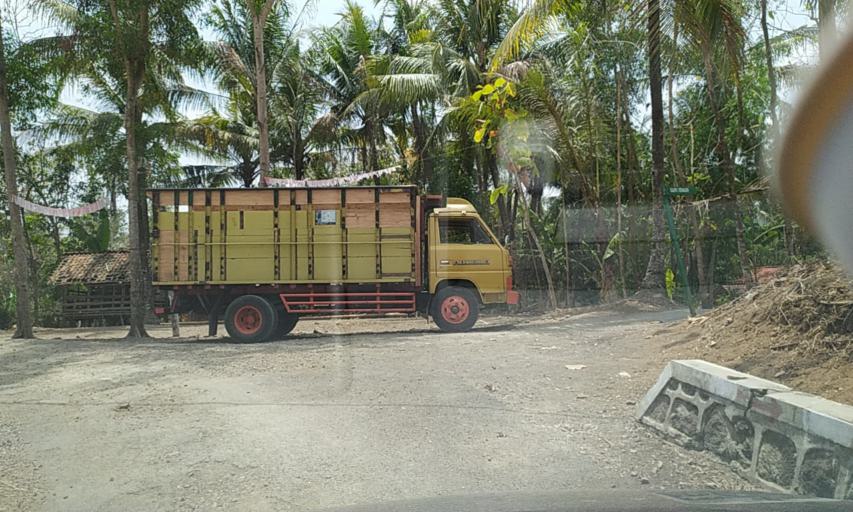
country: ID
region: Central Java
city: Sidakaya
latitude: -7.5657
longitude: 108.9237
